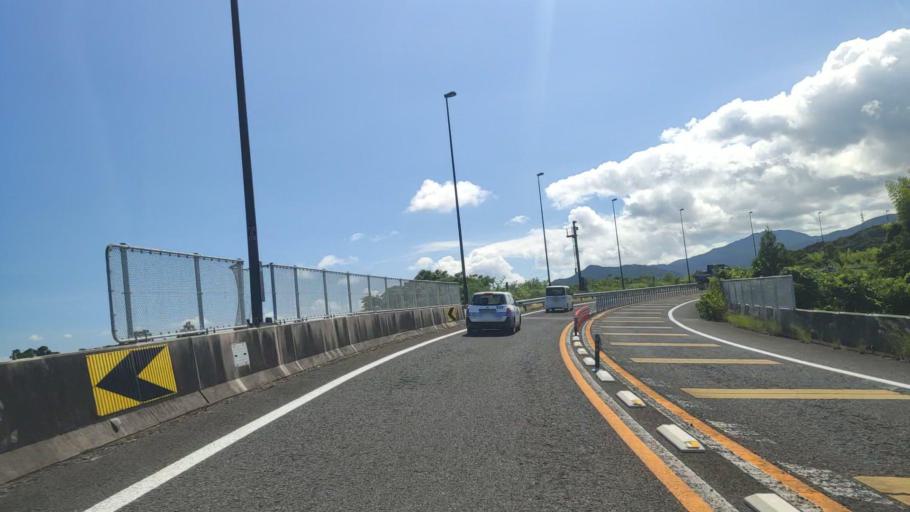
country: JP
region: Wakayama
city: Shingu
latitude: 33.6922
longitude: 135.9845
